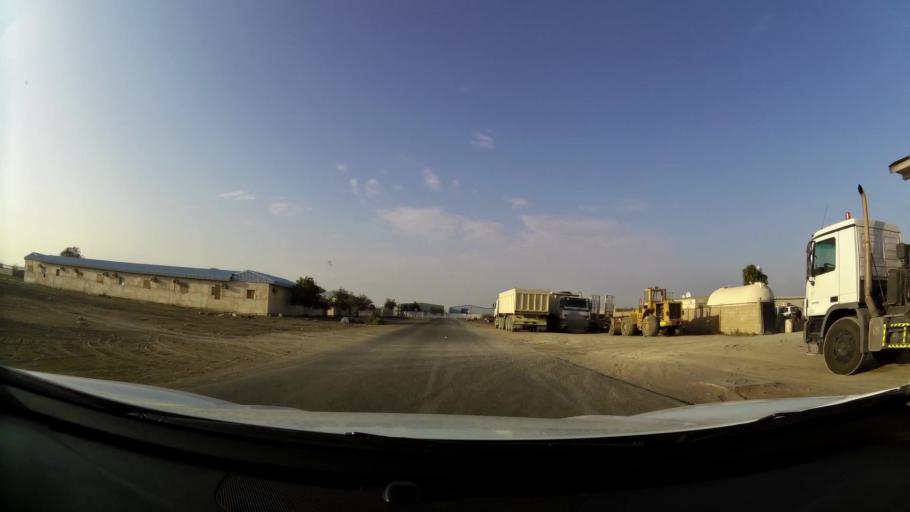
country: AE
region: Abu Dhabi
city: Al Ain
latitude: 24.1471
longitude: 55.8418
